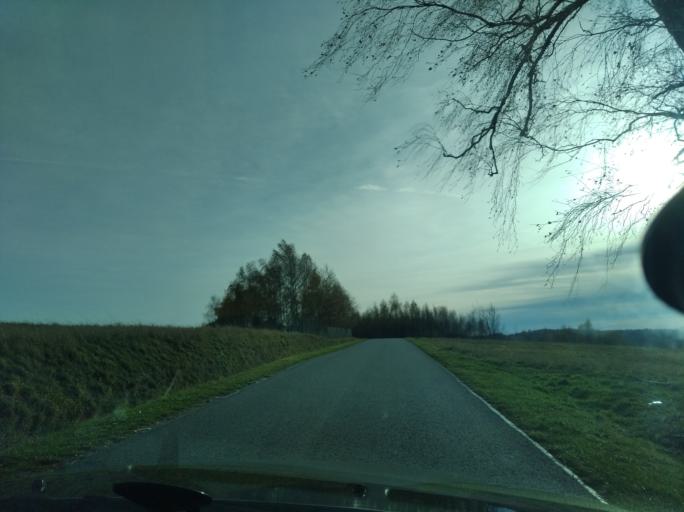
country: PL
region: Subcarpathian Voivodeship
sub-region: Powiat rzeszowski
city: Siedliska
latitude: 49.9349
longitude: 21.9603
